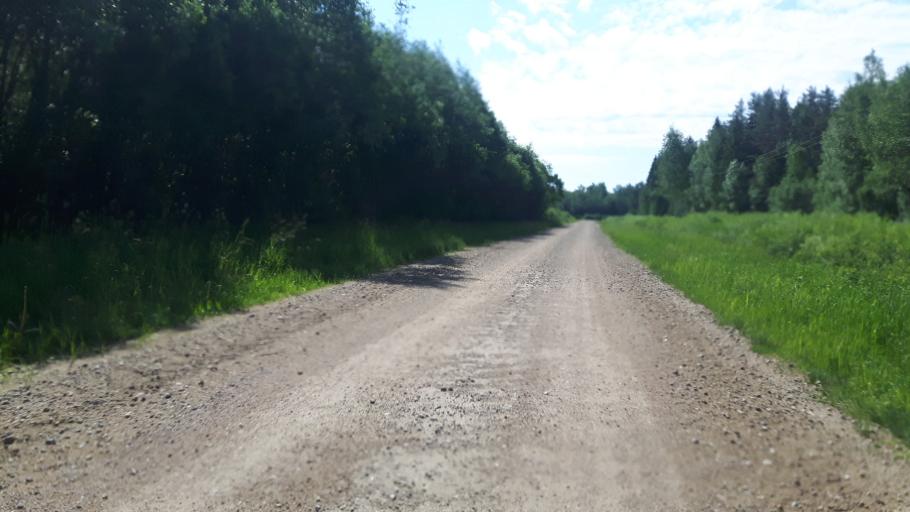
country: EE
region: Paernumaa
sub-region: Vaendra vald (alev)
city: Vandra
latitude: 58.6950
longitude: 25.0318
